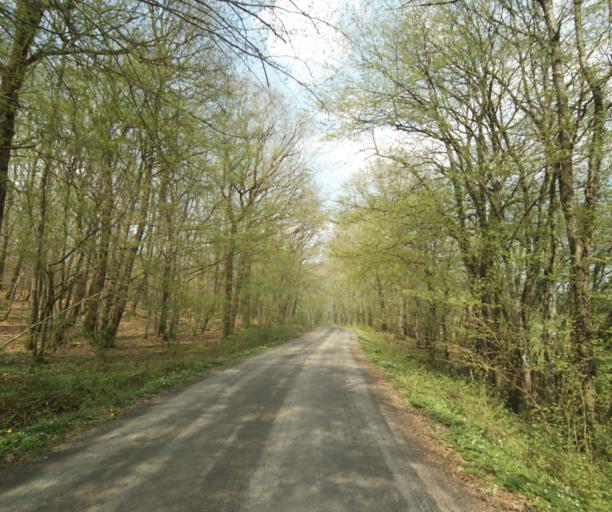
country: FR
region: Bourgogne
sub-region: Departement de Saone-et-Loire
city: Charolles
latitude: 46.4635
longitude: 4.3470
